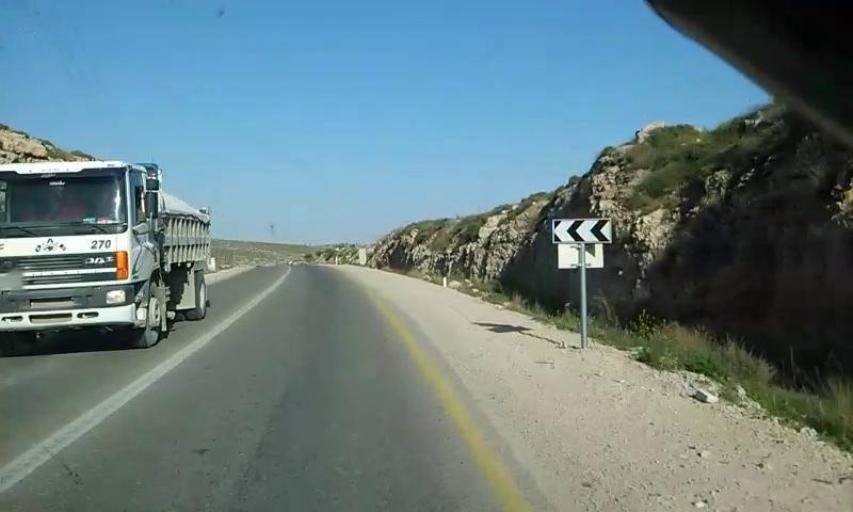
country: PS
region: West Bank
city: Qalqas
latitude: 31.4970
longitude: 35.0940
